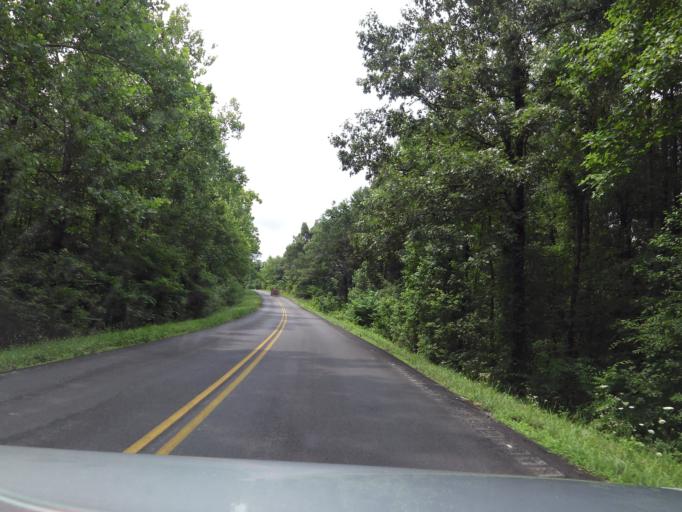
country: US
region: Kentucky
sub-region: Hopkins County
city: Madisonville
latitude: 37.3052
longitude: -87.3677
